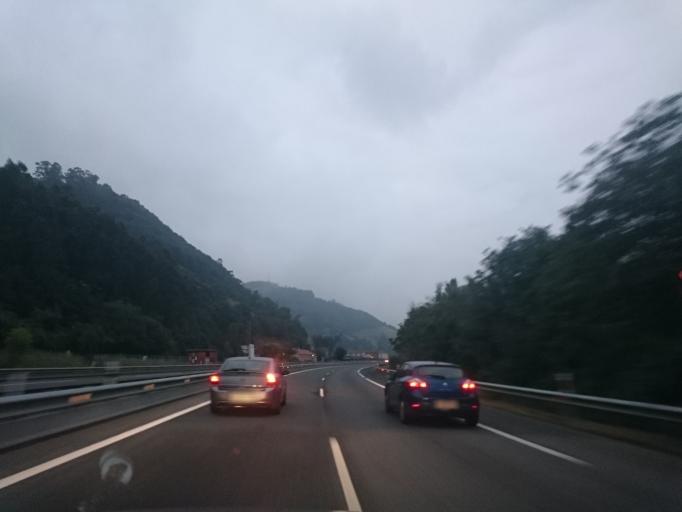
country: ES
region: Asturias
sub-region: Province of Asturias
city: Mieres
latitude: 43.2189
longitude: -5.7836
